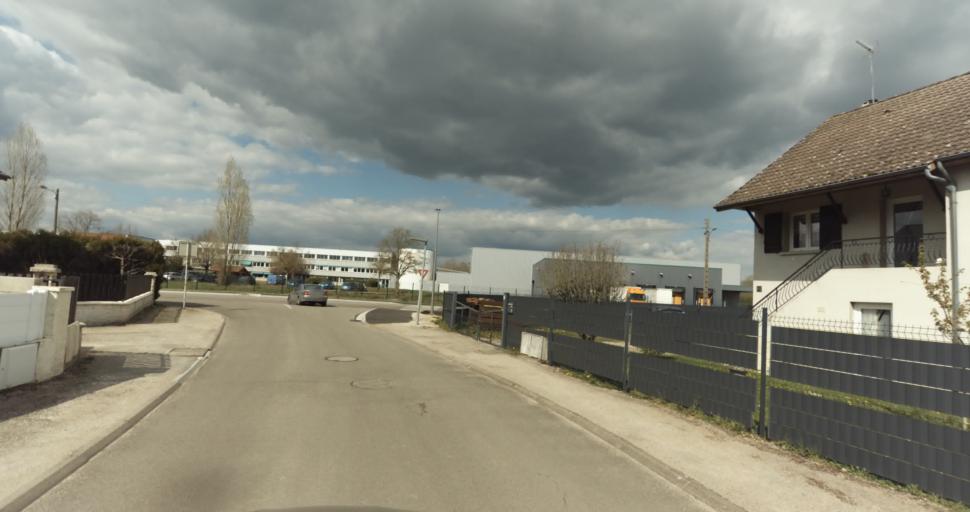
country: FR
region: Bourgogne
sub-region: Departement de la Cote-d'Or
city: Auxonne
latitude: 47.1905
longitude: 5.4134
